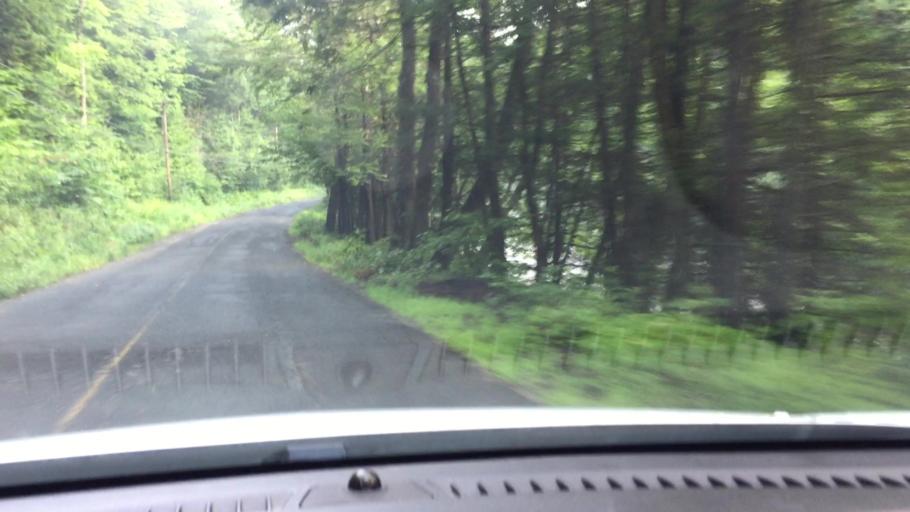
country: US
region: Massachusetts
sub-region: Hampshire County
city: Chesterfield
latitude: 42.3080
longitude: -72.9114
